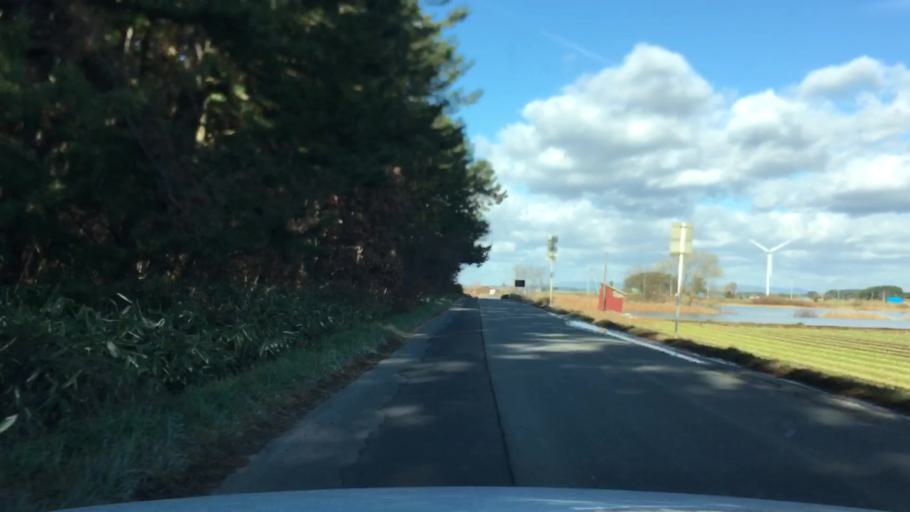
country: JP
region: Aomori
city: Shimokizukuri
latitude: 40.8498
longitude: 140.2999
